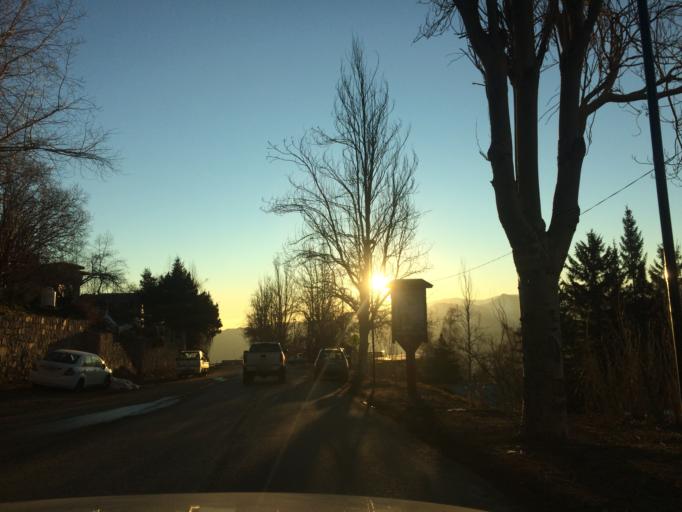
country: CL
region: Santiago Metropolitan
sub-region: Provincia de Santiago
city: Villa Presidente Frei, Nunoa, Santiago, Chile
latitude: -33.3505
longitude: -70.3115
